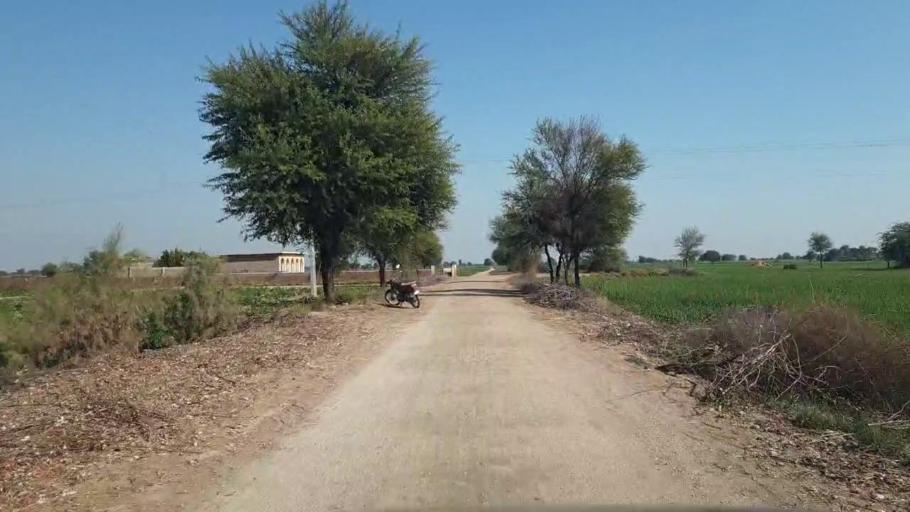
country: PK
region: Sindh
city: Shahpur Chakar
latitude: 26.1181
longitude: 68.6497
